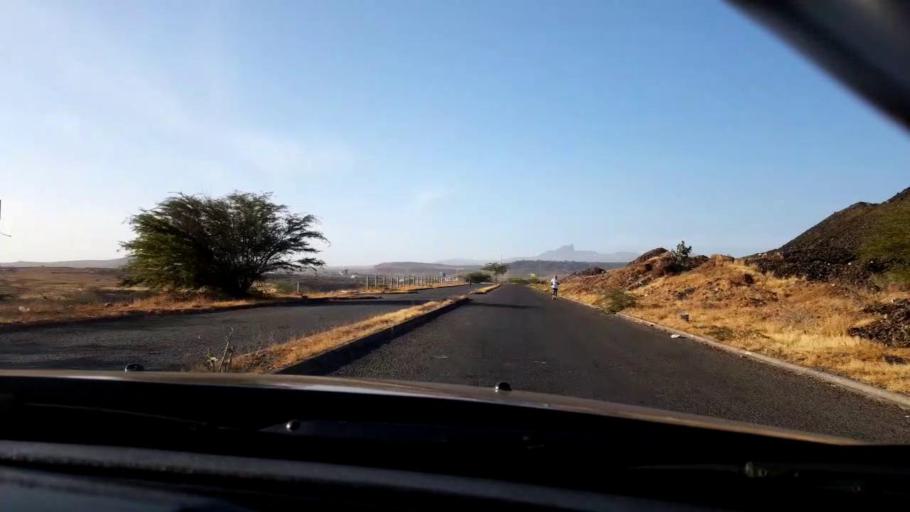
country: CV
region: Praia
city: Praia
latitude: 14.9141
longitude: -23.5401
